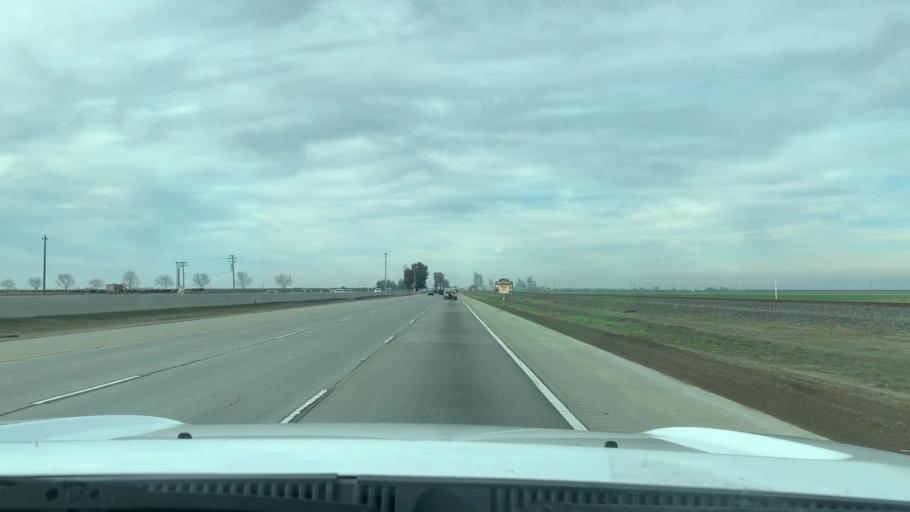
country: US
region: California
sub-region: Tulare County
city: London
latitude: 36.4213
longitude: -119.4674
